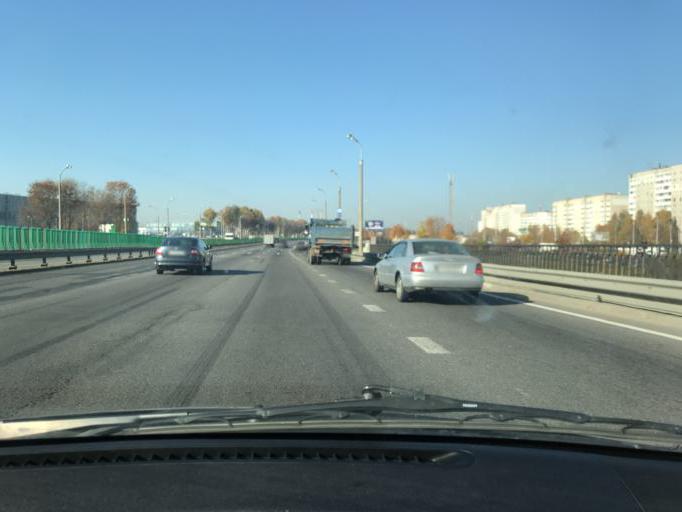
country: BY
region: Minsk
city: Malinovka
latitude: 53.8490
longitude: 27.4387
